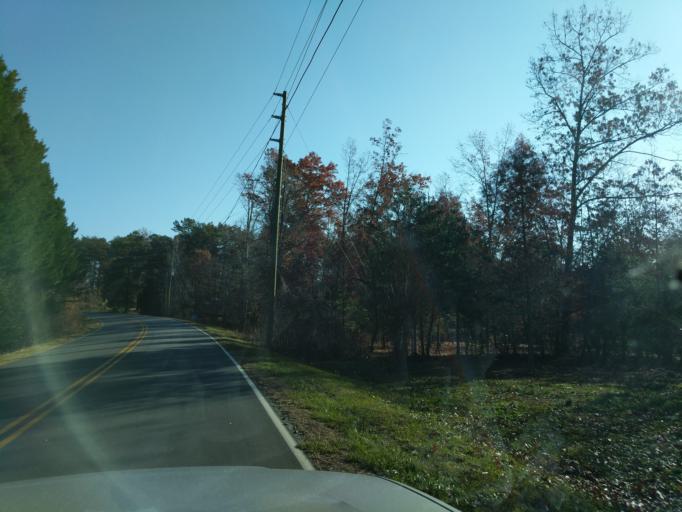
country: US
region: North Carolina
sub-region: Polk County
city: Columbus
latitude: 35.2550
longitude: -82.0777
